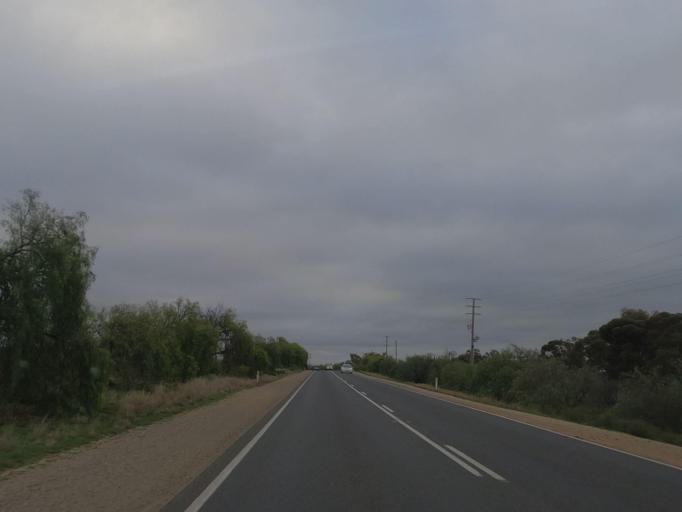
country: AU
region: Victoria
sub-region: Swan Hill
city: Swan Hill
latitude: -35.4473
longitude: 143.6213
